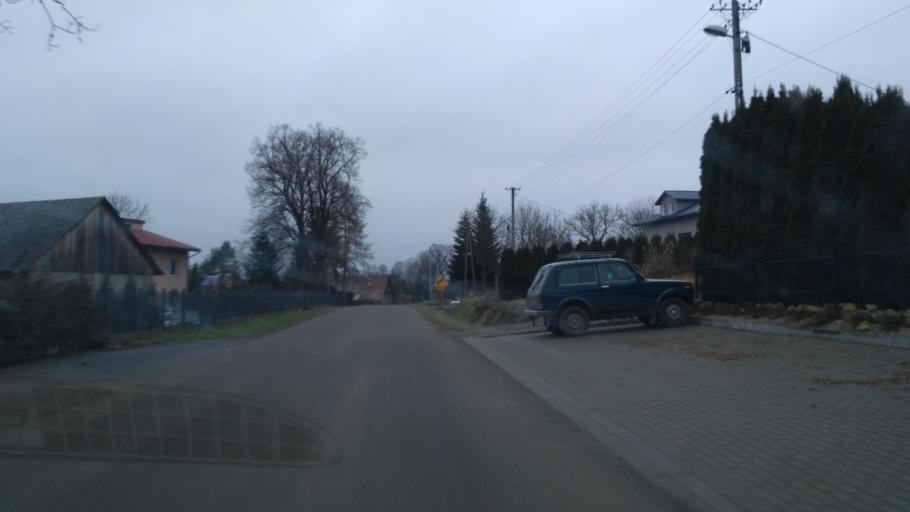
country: PL
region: Subcarpathian Voivodeship
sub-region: Powiat jaroslawski
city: Pruchnik
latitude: 49.9260
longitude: 22.5350
